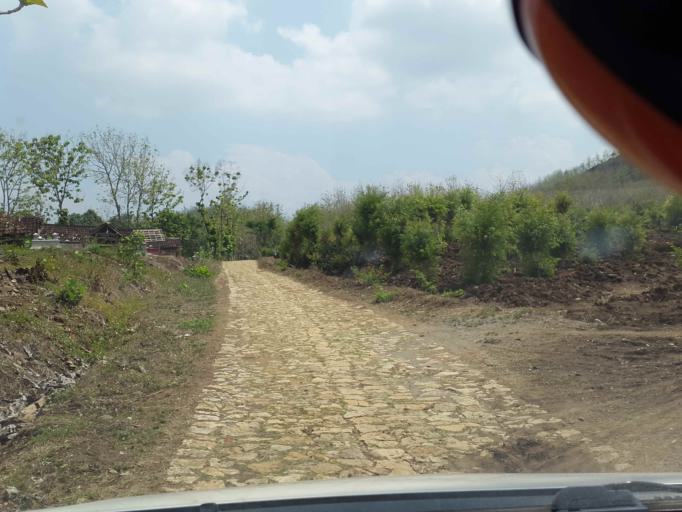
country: ID
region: East Java
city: Ponorogo
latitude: -7.8167
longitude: 111.3197
